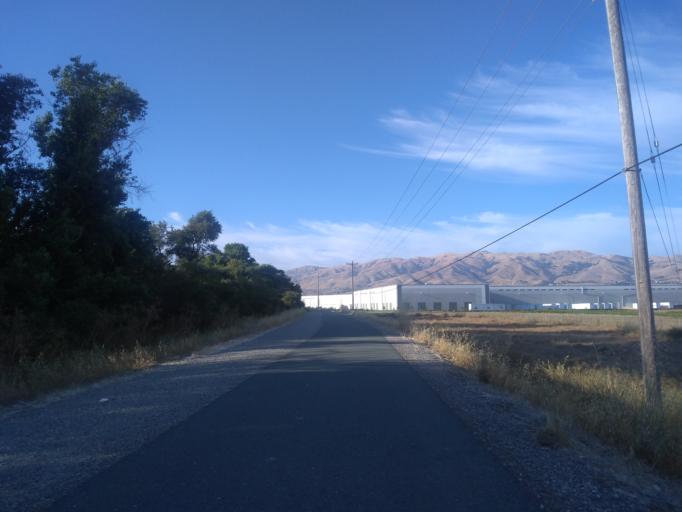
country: US
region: California
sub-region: Santa Clara County
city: Milpitas
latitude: 37.4320
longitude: -121.9275
